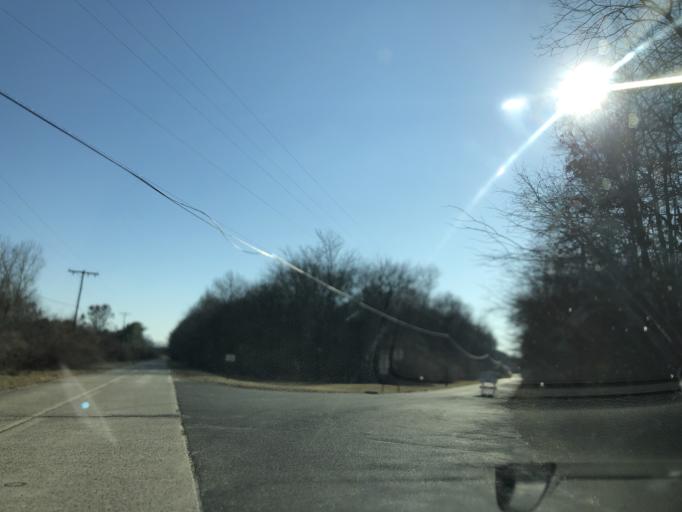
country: US
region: Pennsylvania
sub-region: Delaware County
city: Chester
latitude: 39.8084
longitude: -75.3566
